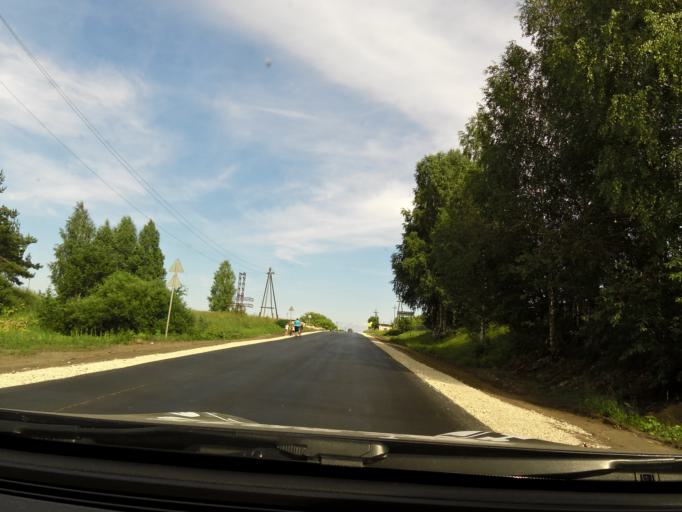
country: RU
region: Kirov
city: Slobodskoy
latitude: 58.7818
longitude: 50.4220
